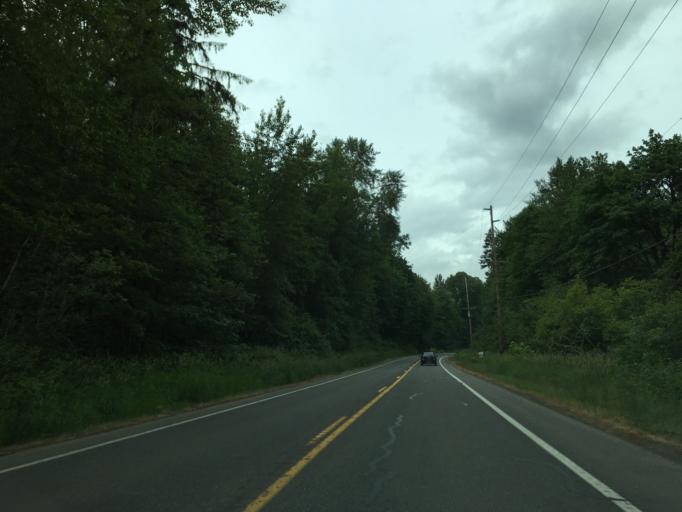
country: US
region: Washington
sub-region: Whatcom County
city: Peaceful Valley
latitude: 48.8780
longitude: -122.1572
